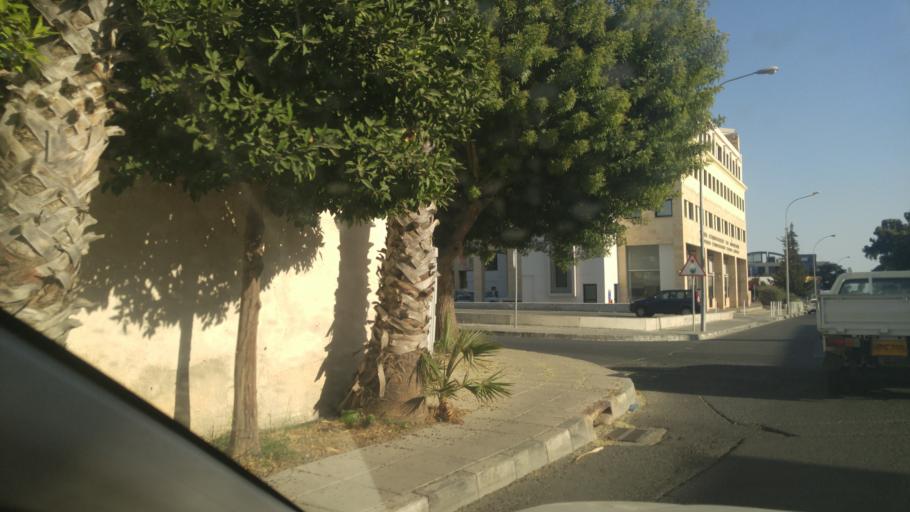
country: CY
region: Limassol
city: Limassol
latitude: 34.6683
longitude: 33.0242
